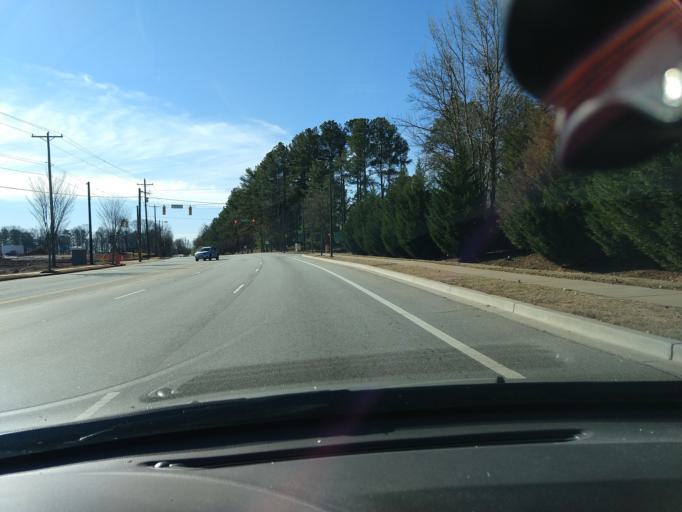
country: US
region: South Carolina
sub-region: Greenville County
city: Mauldin
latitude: 34.7989
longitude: -82.3464
